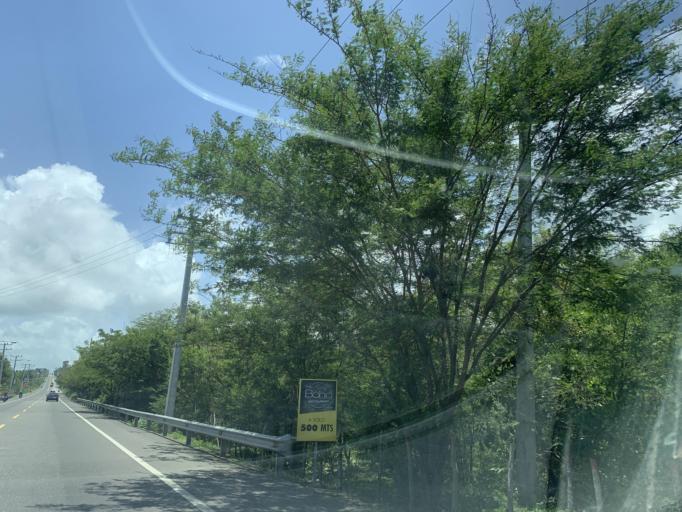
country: DO
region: Puerto Plata
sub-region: Puerto Plata
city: Puerto Plata
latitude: 19.7423
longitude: -70.6344
